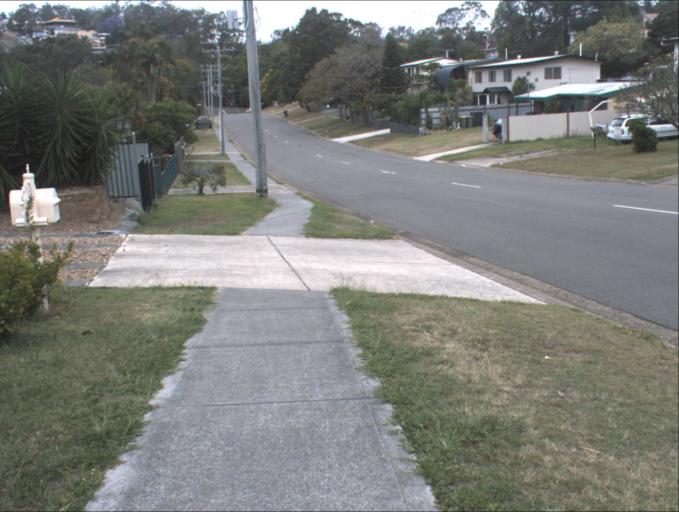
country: AU
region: Queensland
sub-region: Logan
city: Beenleigh
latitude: -27.7163
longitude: 153.1871
